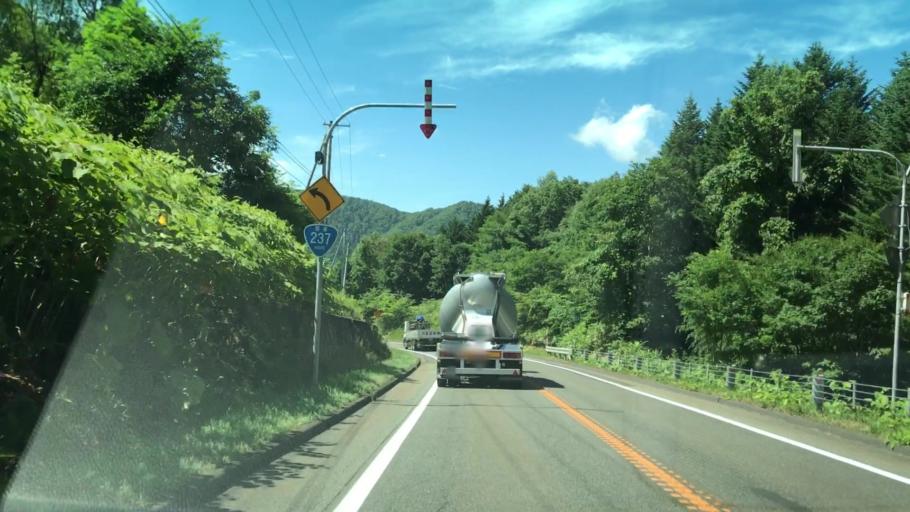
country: JP
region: Hokkaido
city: Shimo-furano
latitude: 42.9001
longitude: 142.4372
